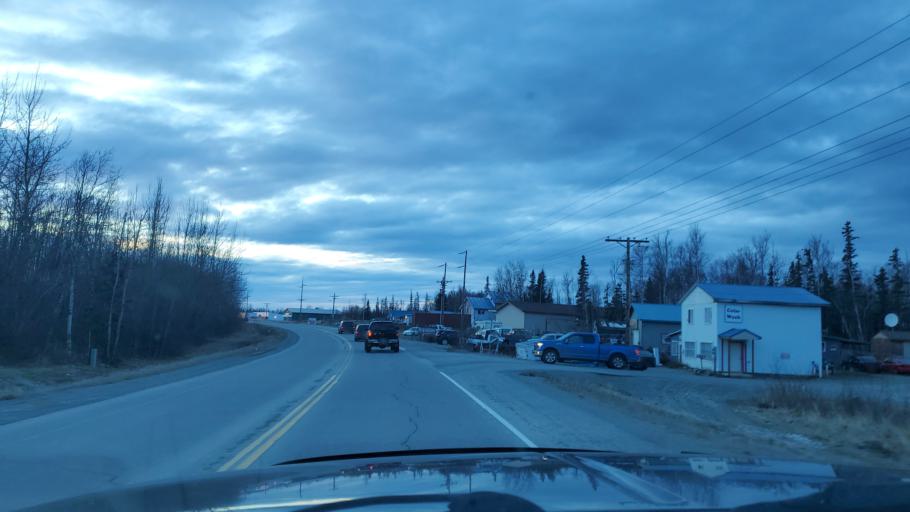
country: US
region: Alaska
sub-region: Matanuska-Susitna Borough
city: Tanaina
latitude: 61.5933
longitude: -149.3902
